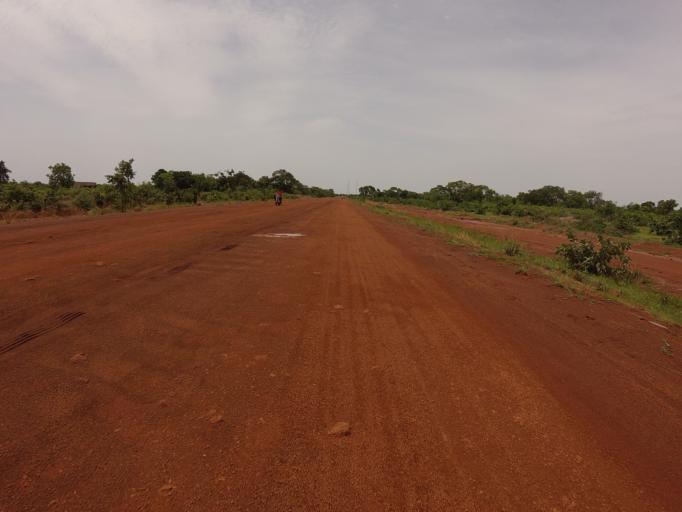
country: GH
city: Kpandae
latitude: 8.8826
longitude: 0.0325
